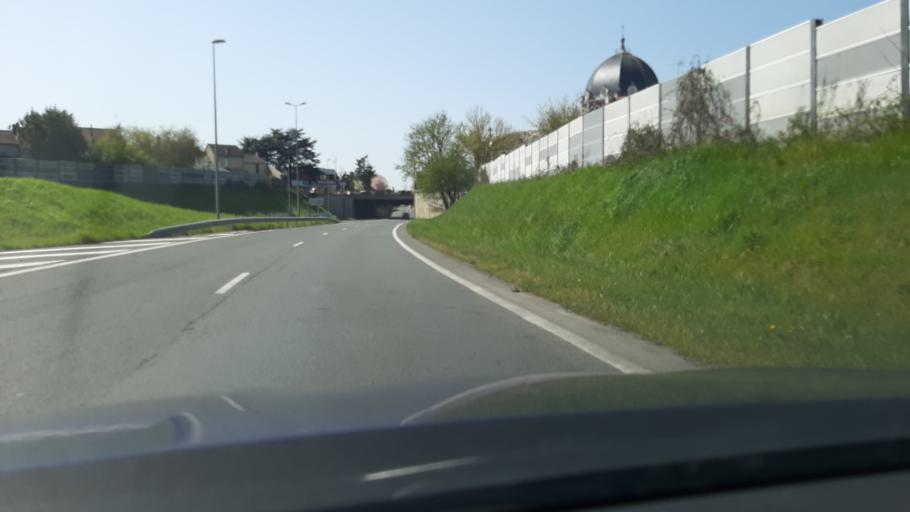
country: FR
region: Pays de la Loire
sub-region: Departement de Maine-et-Loire
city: Angers
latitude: 47.4604
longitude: -0.5192
